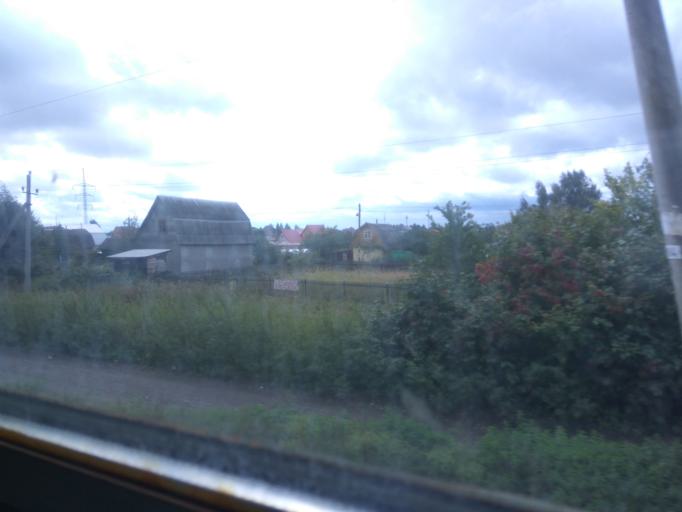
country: RU
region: Moskovskaya
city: Beloozerskiy
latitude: 55.4791
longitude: 38.4103
